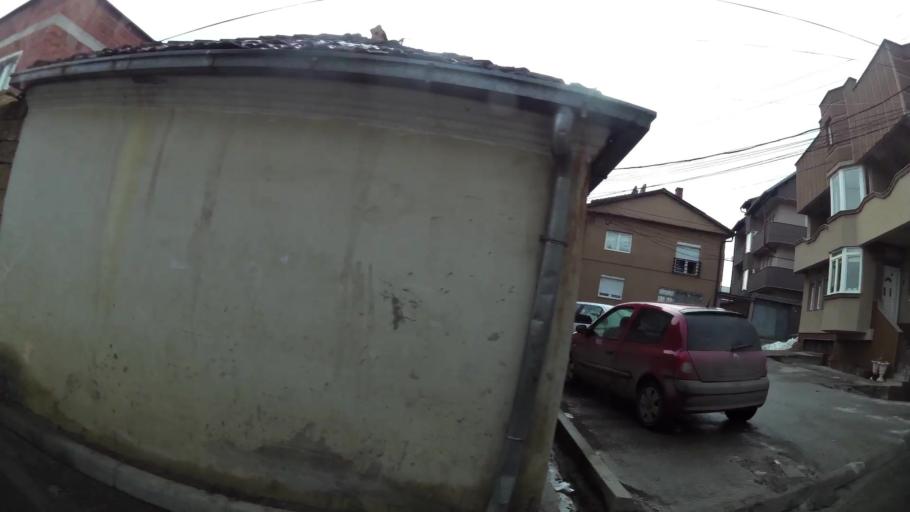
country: XK
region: Pristina
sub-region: Komuna e Prishtines
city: Pristina
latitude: 42.6725
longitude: 21.1602
